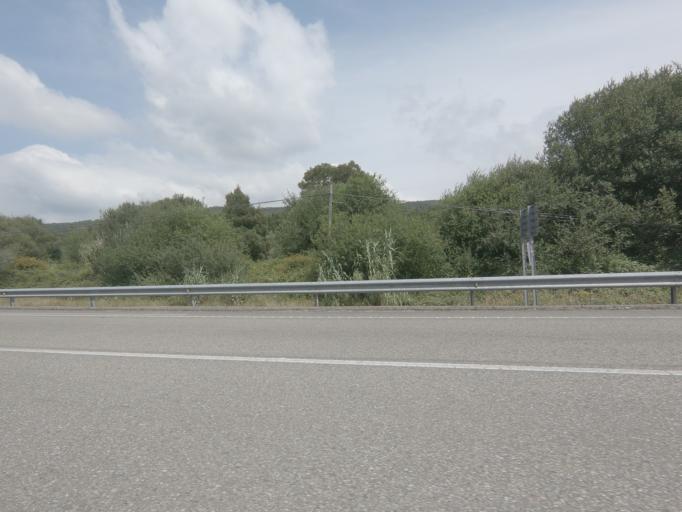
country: ES
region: Galicia
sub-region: Provincia de Pontevedra
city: Tomino
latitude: 42.0256
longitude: -8.7329
